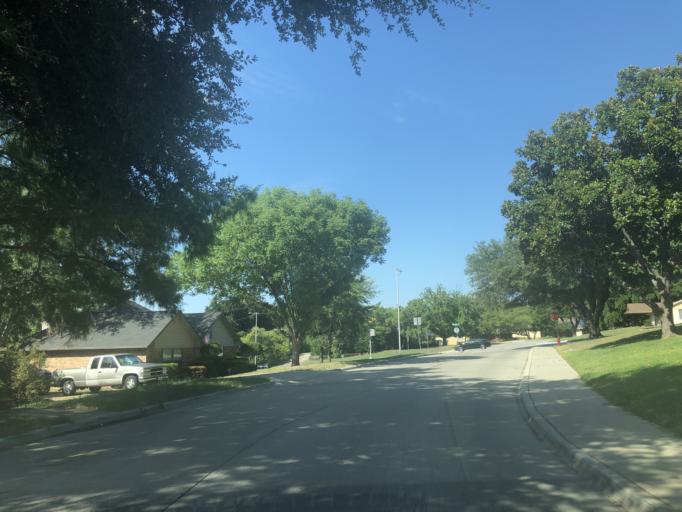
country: US
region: Texas
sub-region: Dallas County
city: Grand Prairie
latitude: 32.7564
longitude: -97.0167
